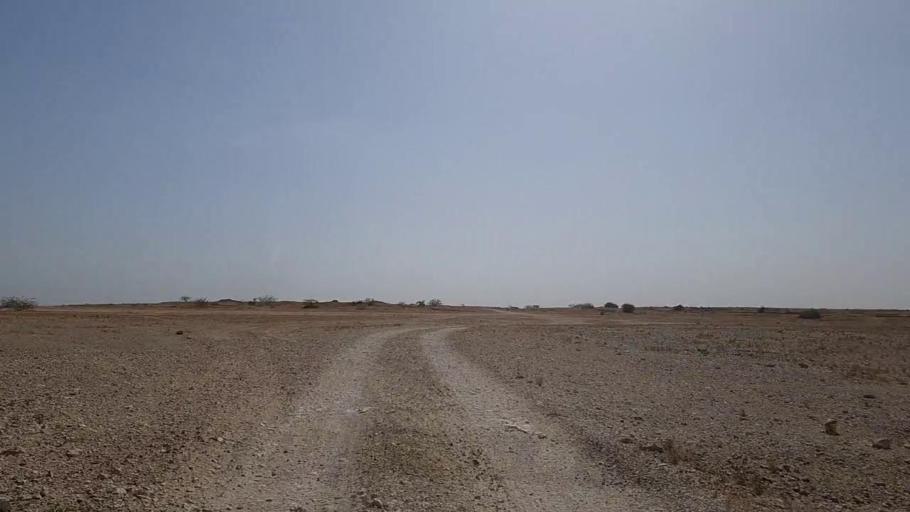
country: PK
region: Sindh
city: Kotri
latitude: 25.1656
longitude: 68.1839
